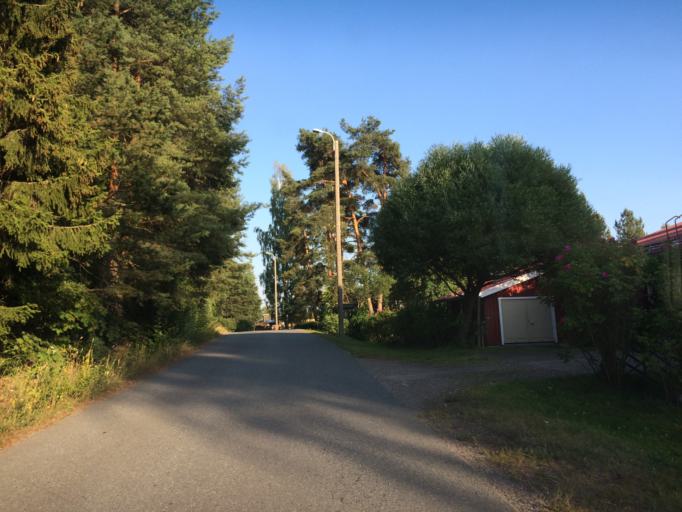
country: FI
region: Haeme
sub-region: Haemeenlinna
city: Parola
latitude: 61.0351
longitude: 24.3928
